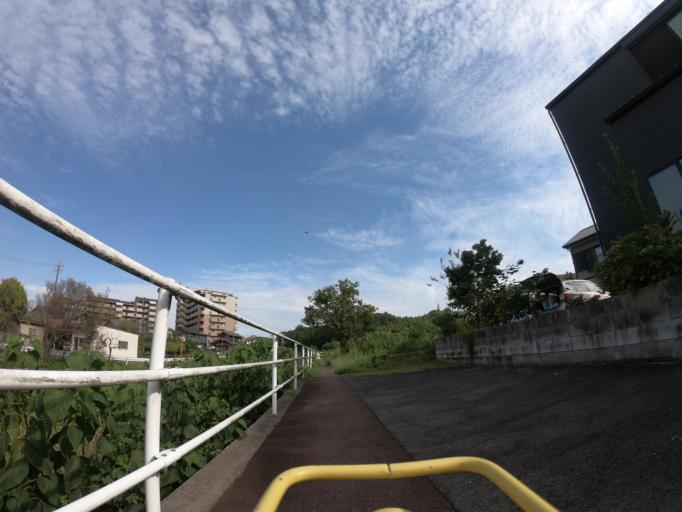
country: JP
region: Aichi
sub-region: Toyota-shi
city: Toyota
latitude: 35.1311
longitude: 137.0516
